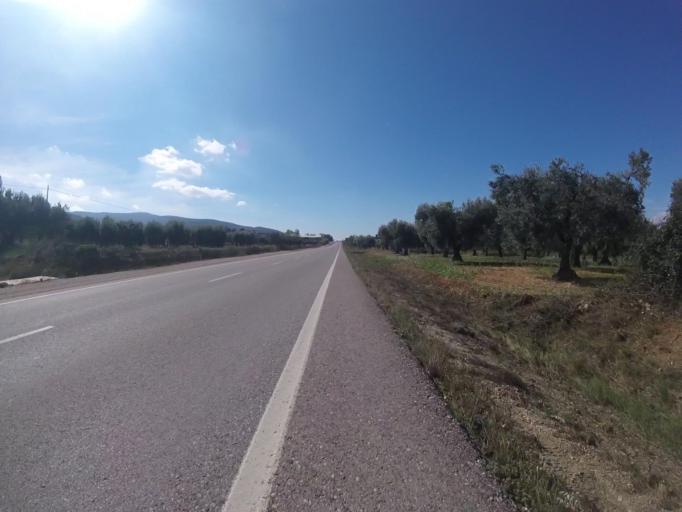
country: ES
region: Valencia
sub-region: Provincia de Castello
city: Albocasser
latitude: 40.3388
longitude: -0.0097
